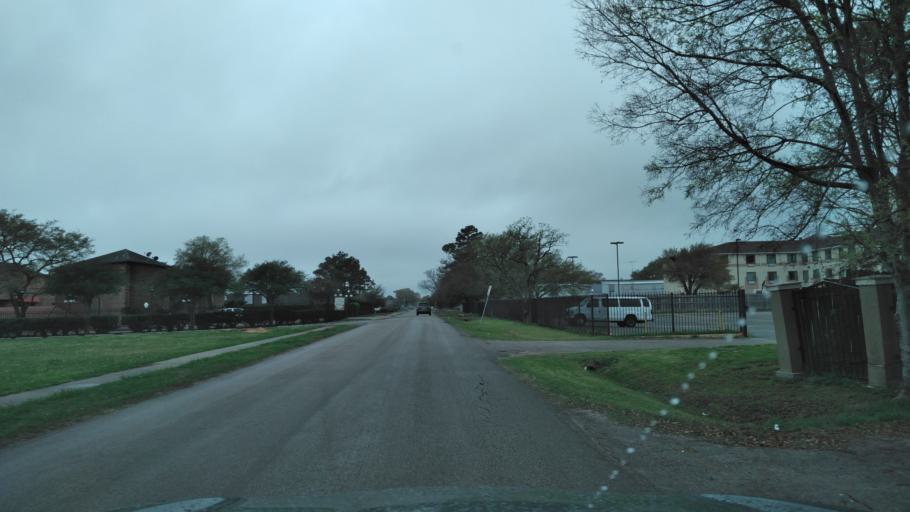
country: US
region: Texas
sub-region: Harris County
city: Piney Point Village
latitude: 29.7307
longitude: -95.4914
